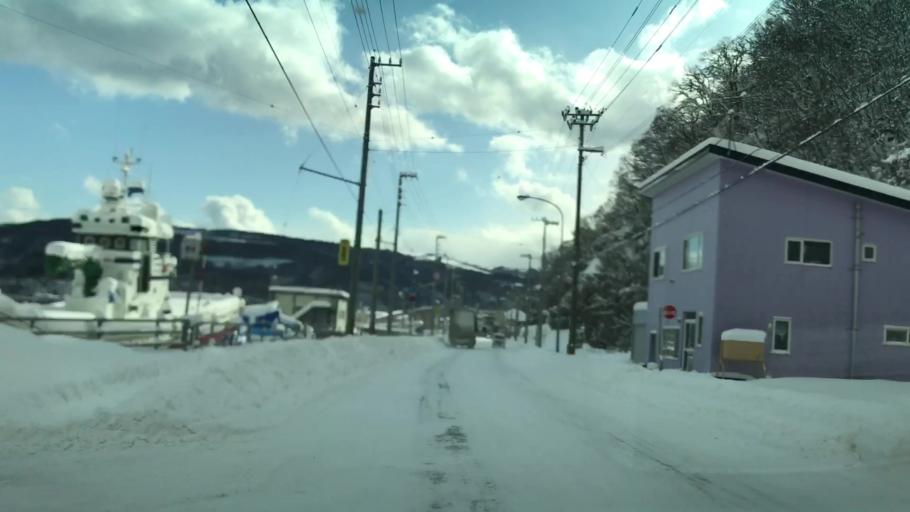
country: JP
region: Hokkaido
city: Yoichi
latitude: 43.2711
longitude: 140.6368
